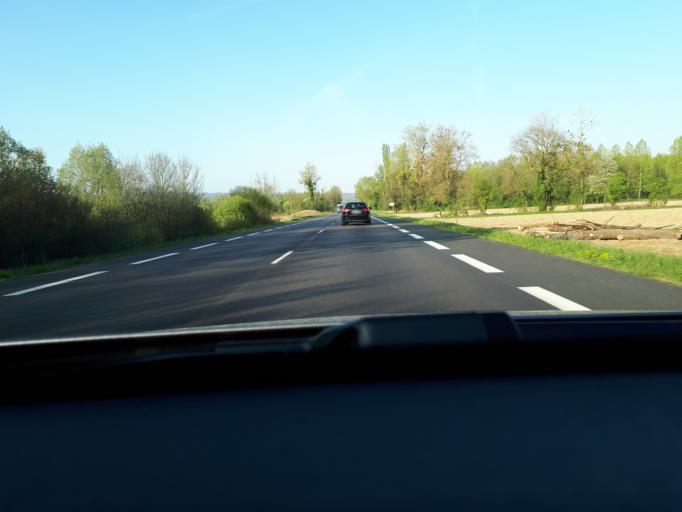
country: FR
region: Rhone-Alpes
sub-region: Departement de l'Isere
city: L'Isle-d'Abeau
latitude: 45.6139
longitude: 5.2639
